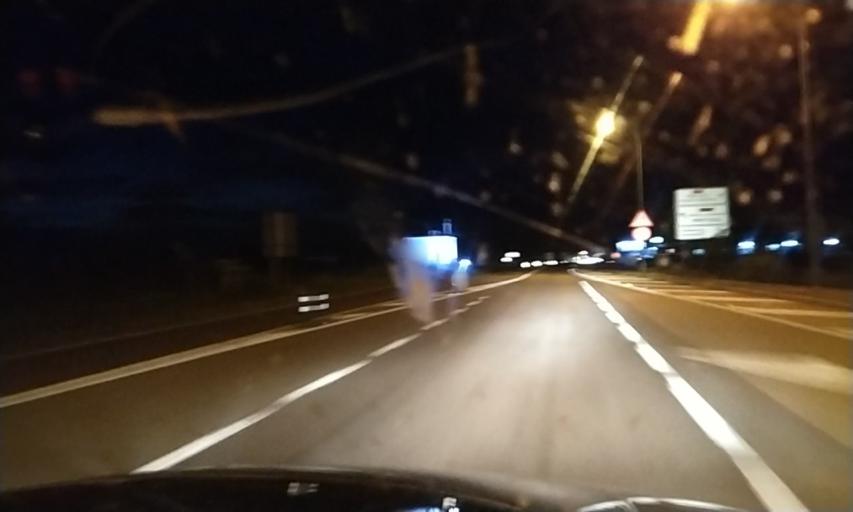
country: ES
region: Extremadura
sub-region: Provincia de Caceres
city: Moraleja
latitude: 40.0590
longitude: -6.6472
